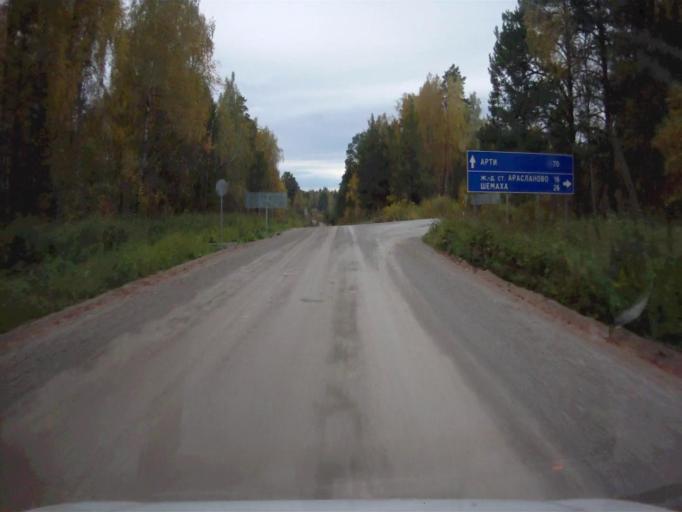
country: RU
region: Chelyabinsk
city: Nyazepetrovsk
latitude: 56.0864
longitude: 59.4185
